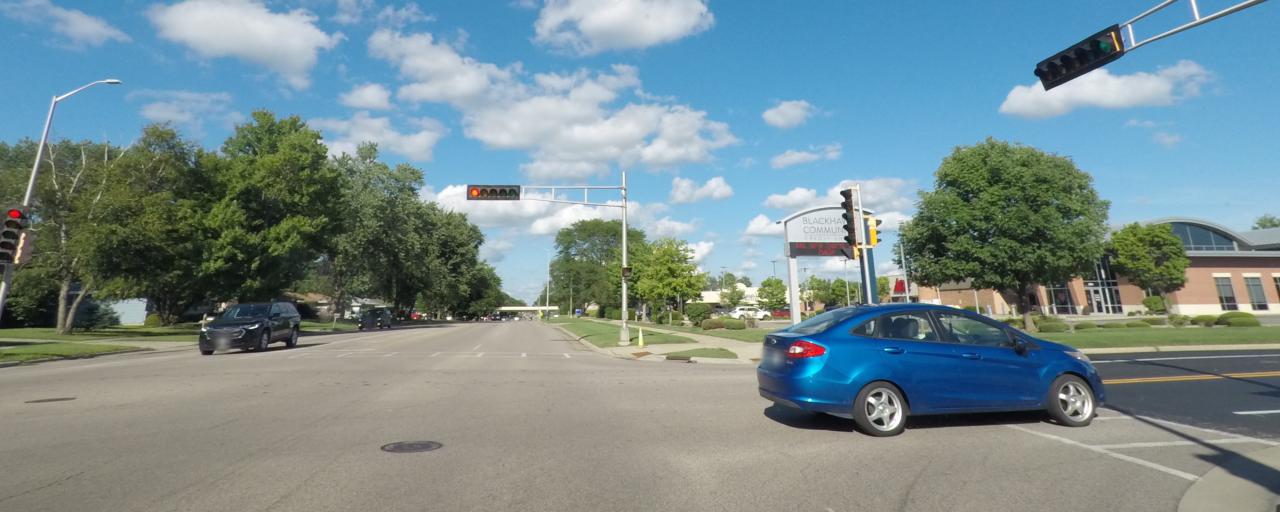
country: US
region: Wisconsin
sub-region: Rock County
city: Janesville
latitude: 42.6955
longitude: -88.9880
